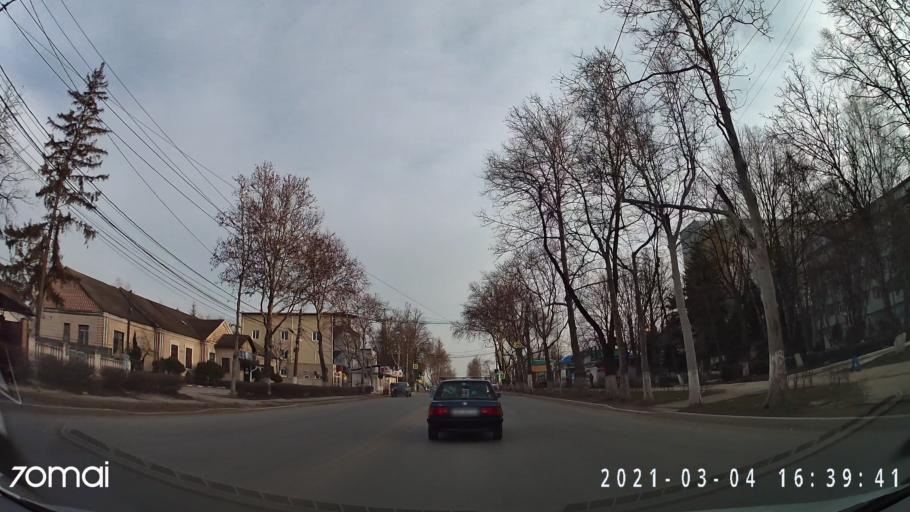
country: MD
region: Balti
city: Balti
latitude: 47.7735
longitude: 27.8978
